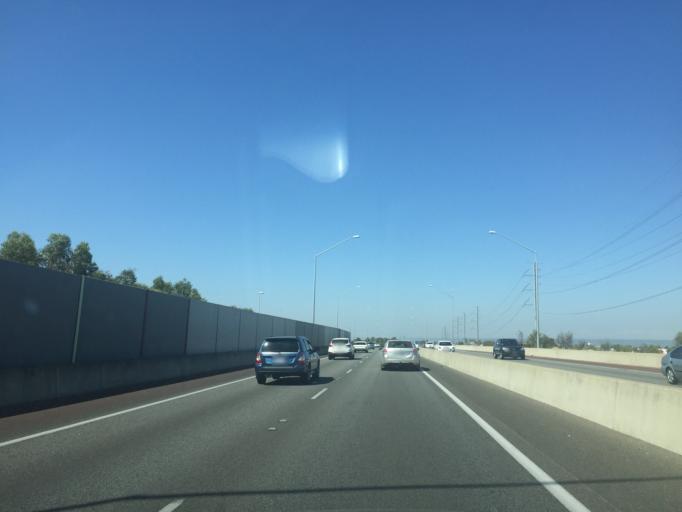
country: AU
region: Western Australia
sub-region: Canning
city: Willetton
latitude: -32.0704
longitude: 115.8886
